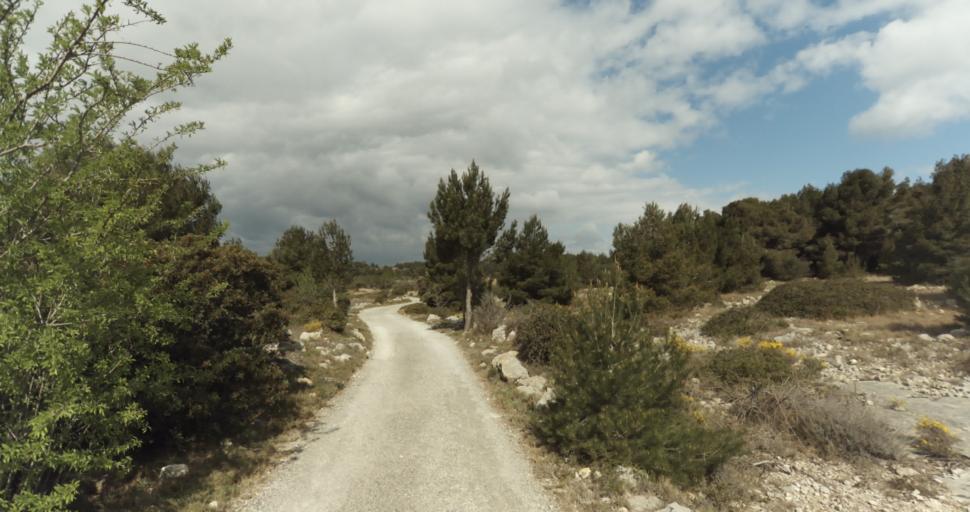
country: FR
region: Languedoc-Roussillon
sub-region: Departement de l'Aude
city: Leucate
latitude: 42.9192
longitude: 3.0487
